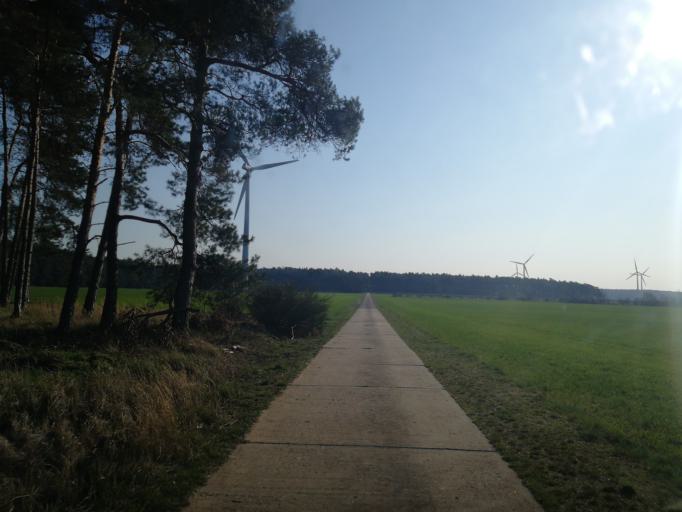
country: DE
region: Brandenburg
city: Drahnsdorf
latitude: 51.8879
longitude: 13.5253
